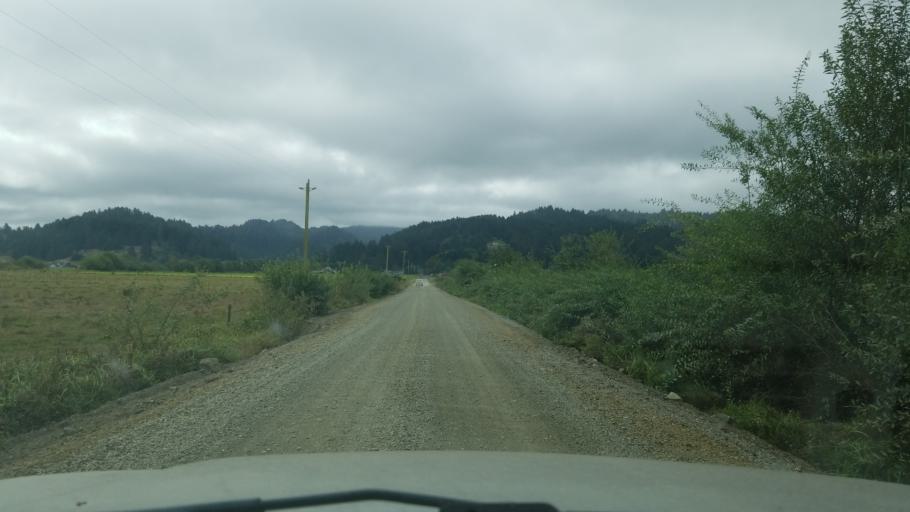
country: US
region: California
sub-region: Humboldt County
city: Ferndale
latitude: 40.5915
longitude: -124.2841
